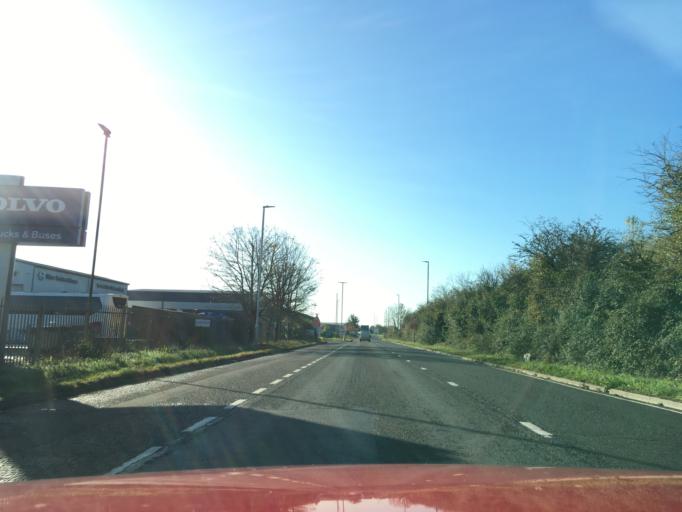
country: GB
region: England
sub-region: Somerset
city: Puriton
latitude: 51.1525
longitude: -2.9883
